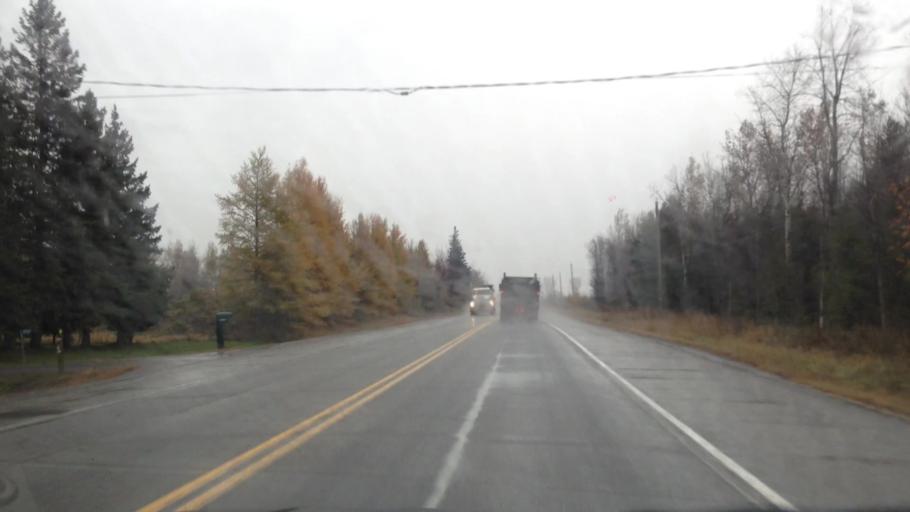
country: CA
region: Ontario
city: Clarence-Rockland
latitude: 45.4180
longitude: -75.4061
